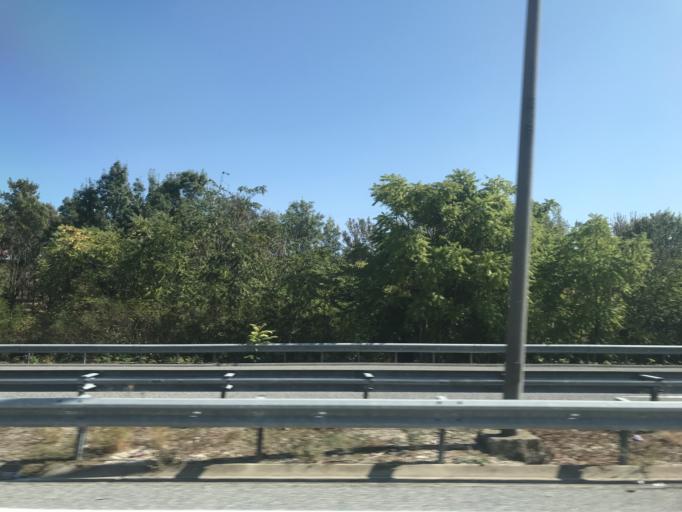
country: TR
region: Kirklareli
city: Luleburgaz
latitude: 41.4401
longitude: 27.3865
